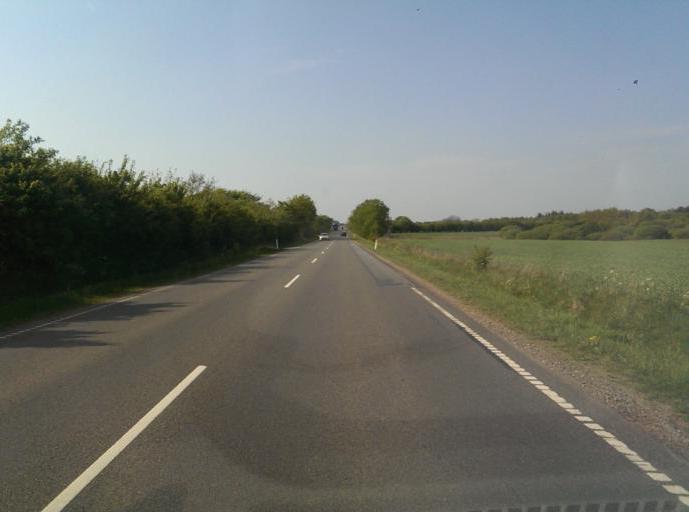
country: DK
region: South Denmark
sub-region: Esbjerg Kommune
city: Tjaereborg
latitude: 55.5094
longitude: 8.5963
